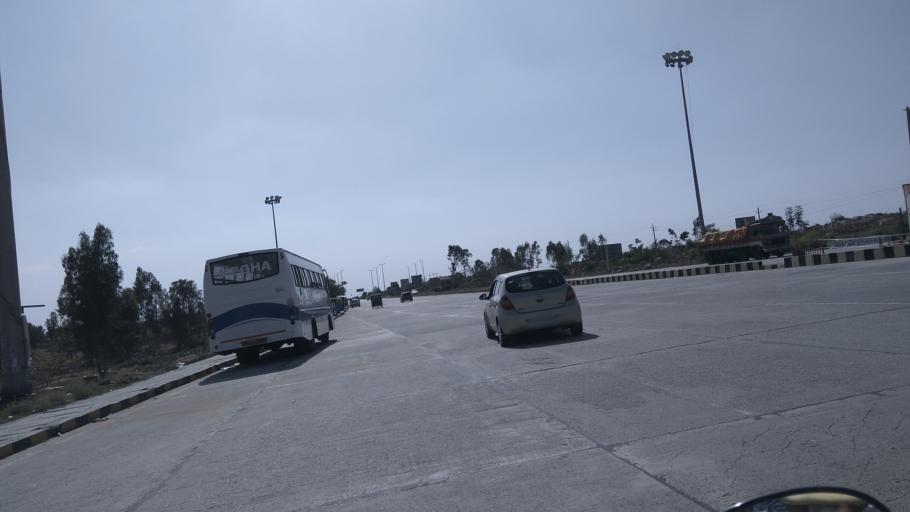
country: IN
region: Karnataka
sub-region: Kolar
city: Mulbagal
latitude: 13.1483
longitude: 78.2904
